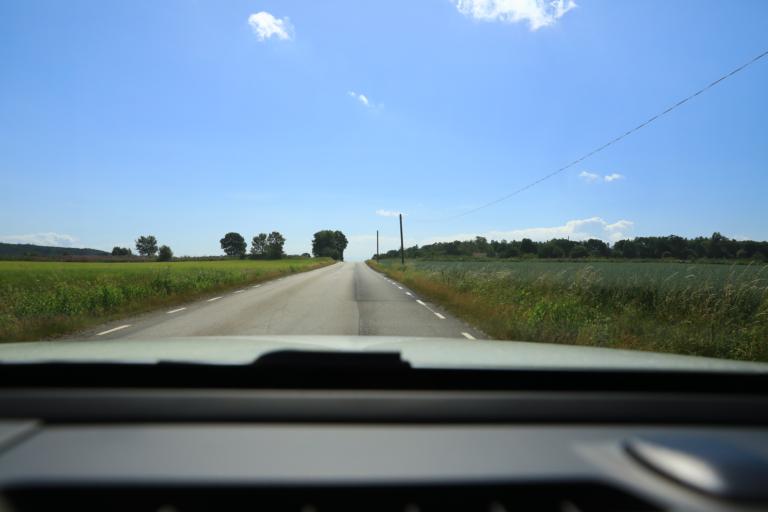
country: SE
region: Halland
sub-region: Varbergs Kommun
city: Tvaaker
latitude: 57.0963
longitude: 12.4083
